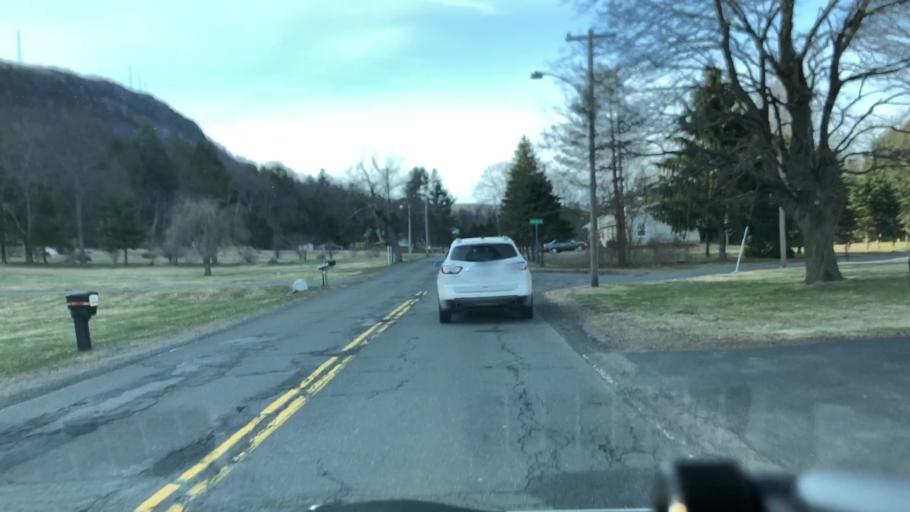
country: US
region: Massachusetts
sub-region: Hampshire County
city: Easthampton
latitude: 42.2549
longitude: -72.6525
